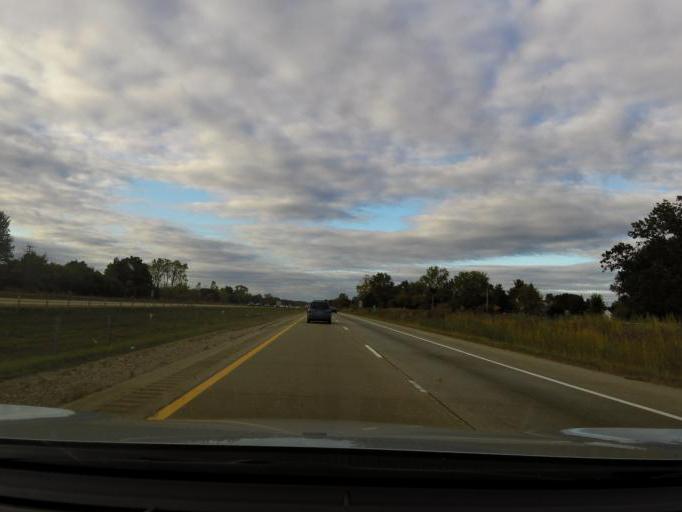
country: US
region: Michigan
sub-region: Genesee County
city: Fenton
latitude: 42.6847
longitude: -83.7602
